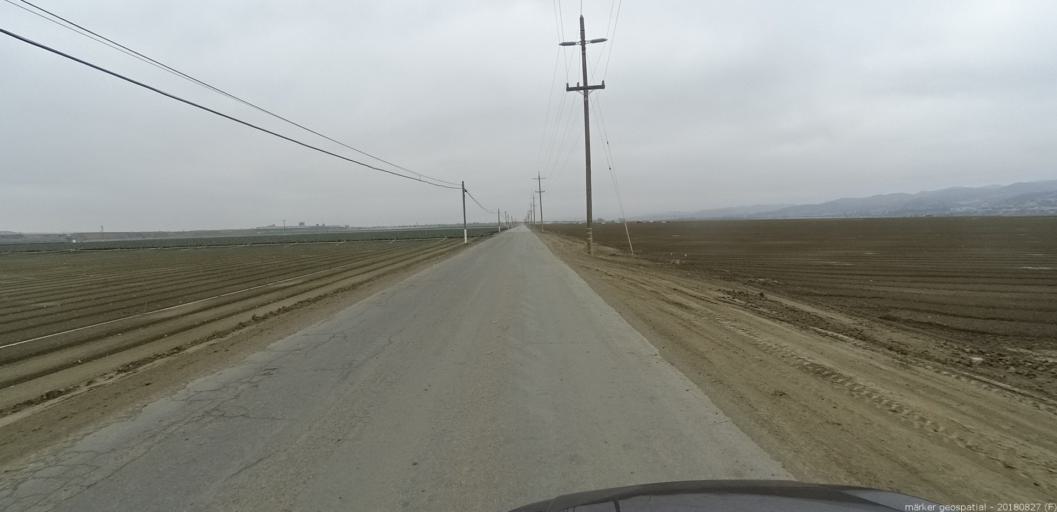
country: US
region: California
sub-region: Monterey County
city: King City
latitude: 36.2455
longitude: -121.1476
